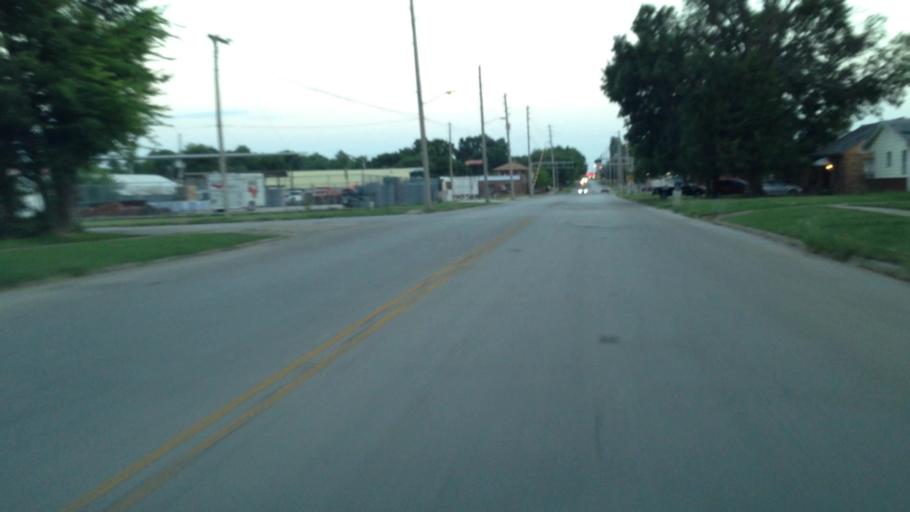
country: US
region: Kansas
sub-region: Montgomery County
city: Independence
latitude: 37.2341
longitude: -95.7108
